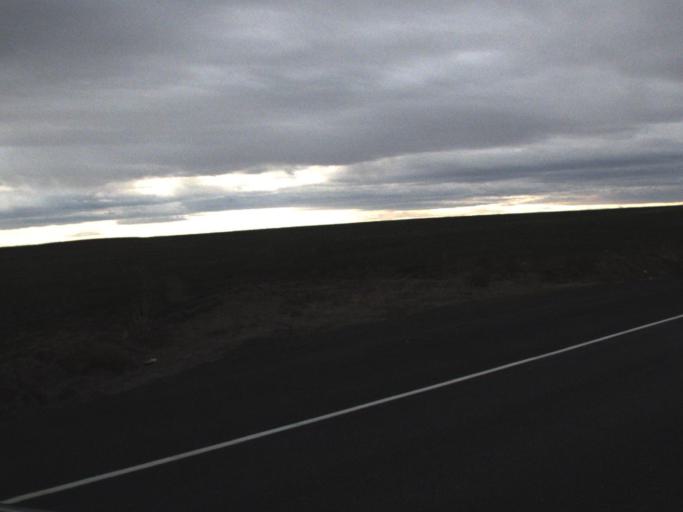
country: US
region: Washington
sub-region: Adams County
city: Ritzville
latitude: 46.7953
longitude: -118.4060
